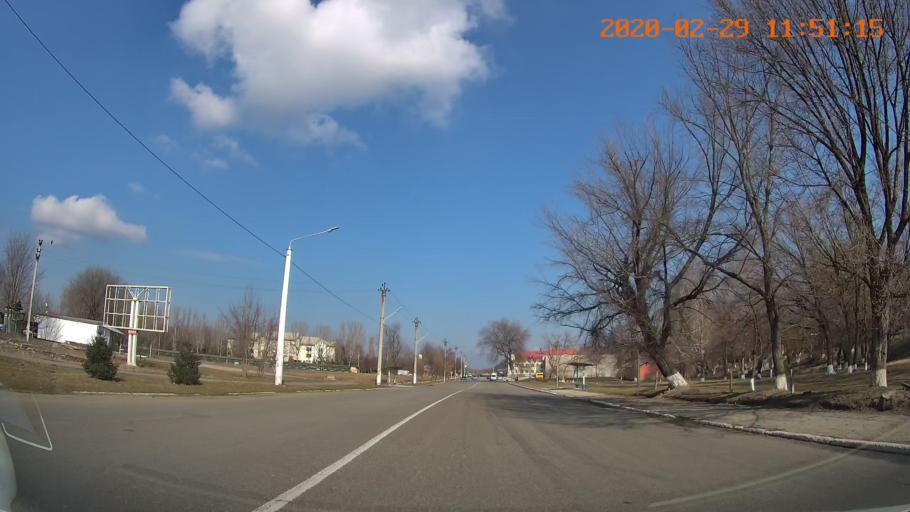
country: MD
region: Telenesti
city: Ribnita
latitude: 47.7639
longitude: 28.9898
